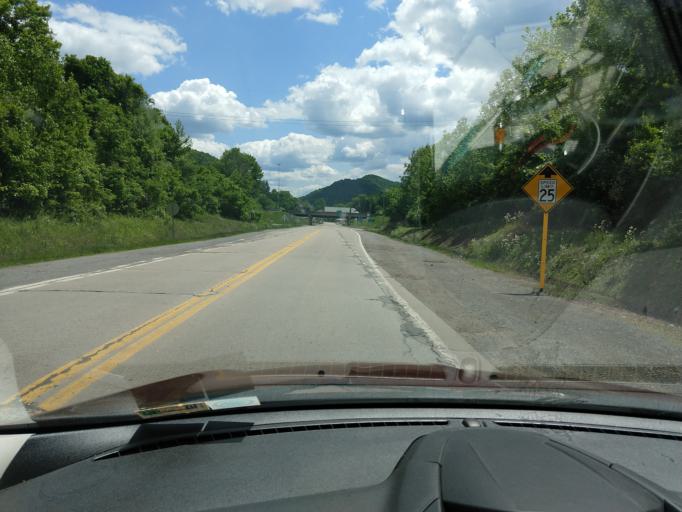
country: US
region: West Virginia
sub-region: Gilmer County
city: Glenville
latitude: 38.8599
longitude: -80.6641
